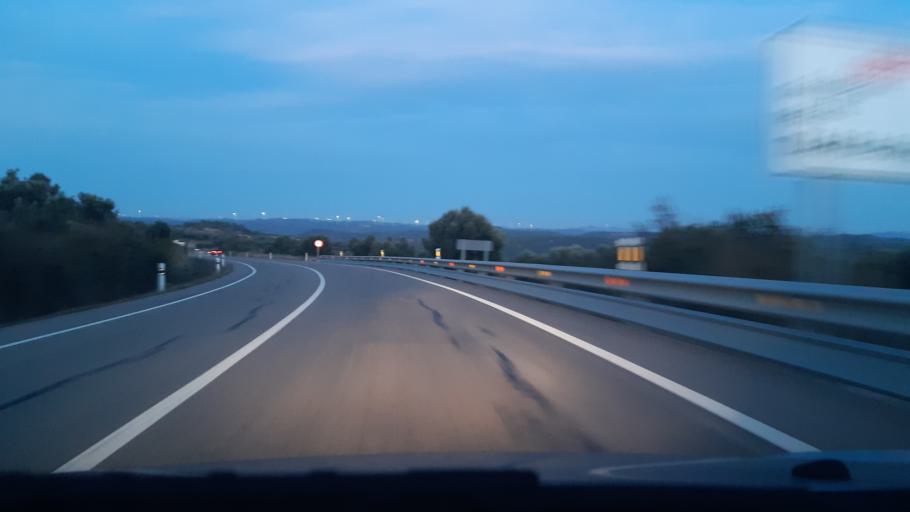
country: ES
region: Aragon
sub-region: Provincia de Teruel
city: Calaceite
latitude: 41.0171
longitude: 0.2007
